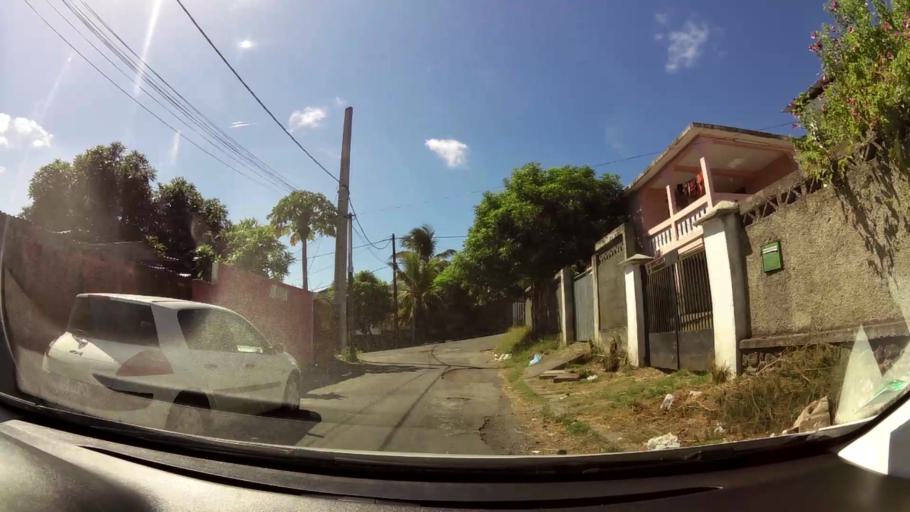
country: YT
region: Pamandzi
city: Pamandzi
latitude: -12.7998
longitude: 45.2794
